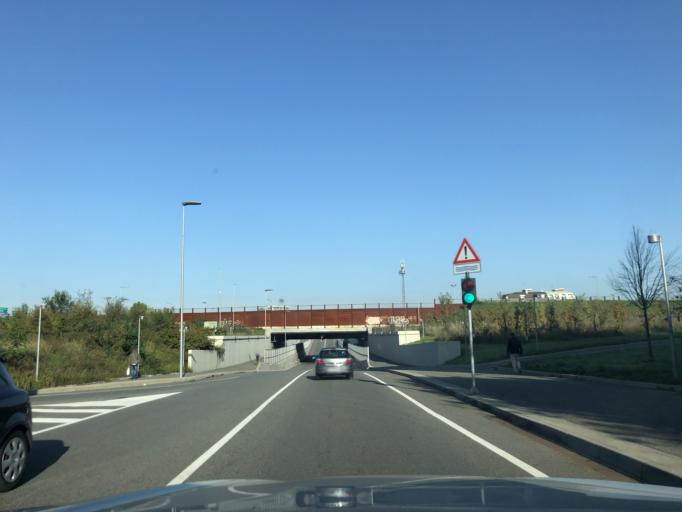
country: IT
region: Lombardy
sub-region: Citta metropolitana di Milano
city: Baranzate
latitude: 45.5289
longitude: 9.1108
